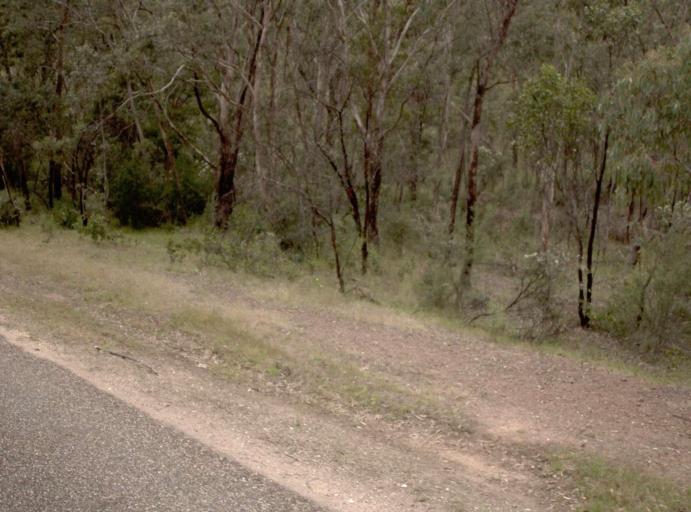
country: AU
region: Victoria
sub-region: East Gippsland
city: Bairnsdale
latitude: -37.5261
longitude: 147.2309
